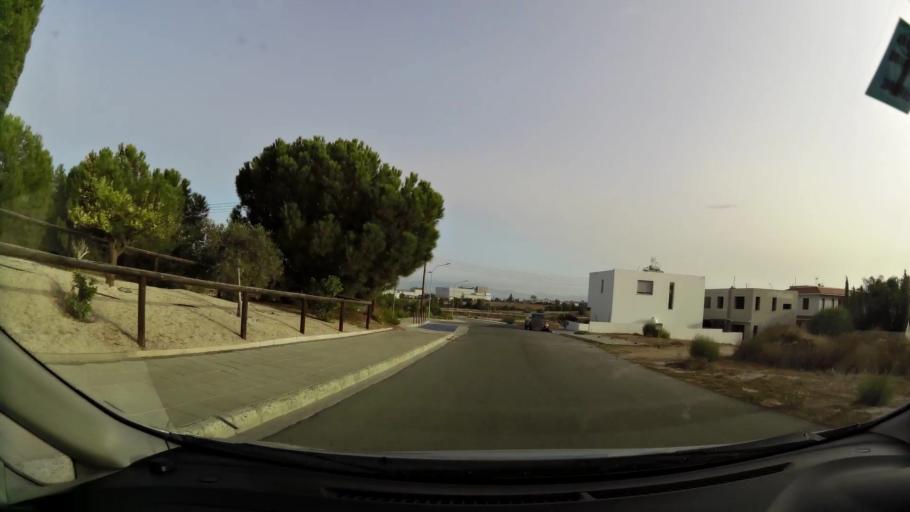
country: CY
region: Lefkosia
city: Geri
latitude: 35.0685
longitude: 33.3790
